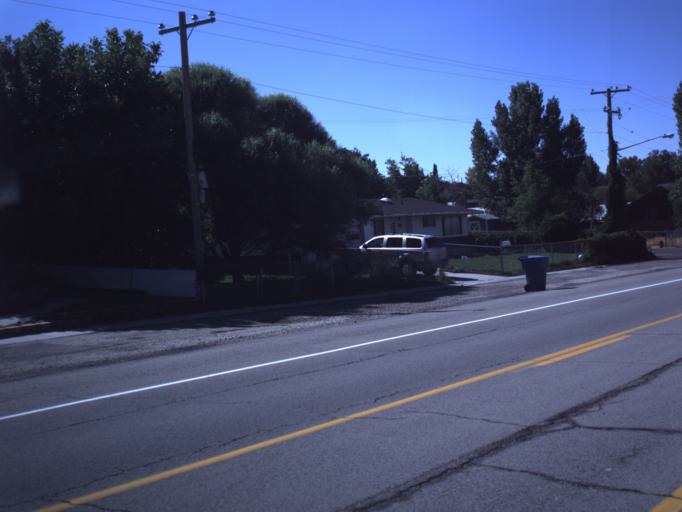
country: US
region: Utah
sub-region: Tooele County
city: Tooele
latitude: 40.4559
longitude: -112.3598
